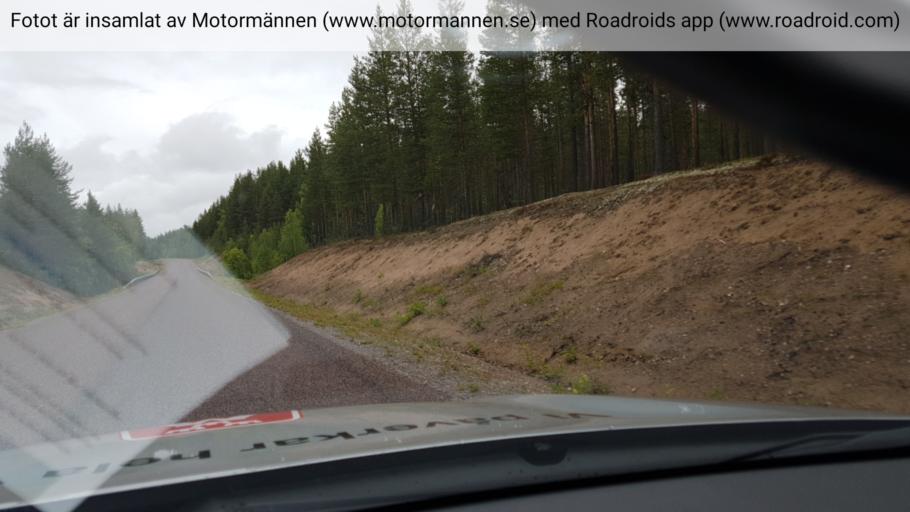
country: SE
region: Norrbotten
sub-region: Gallivare Kommun
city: Gaellivare
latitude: 66.5224
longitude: 20.5416
